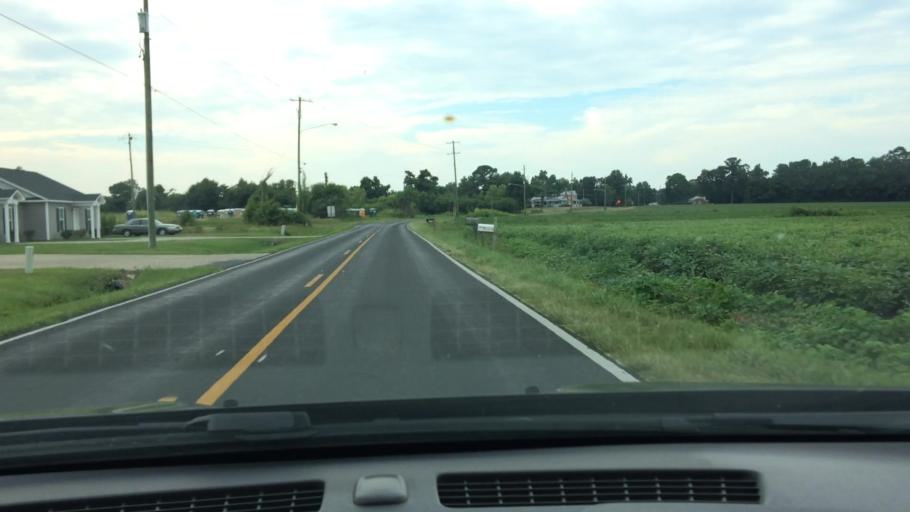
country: US
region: North Carolina
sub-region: Pitt County
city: Ayden
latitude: 35.4557
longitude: -77.4140
